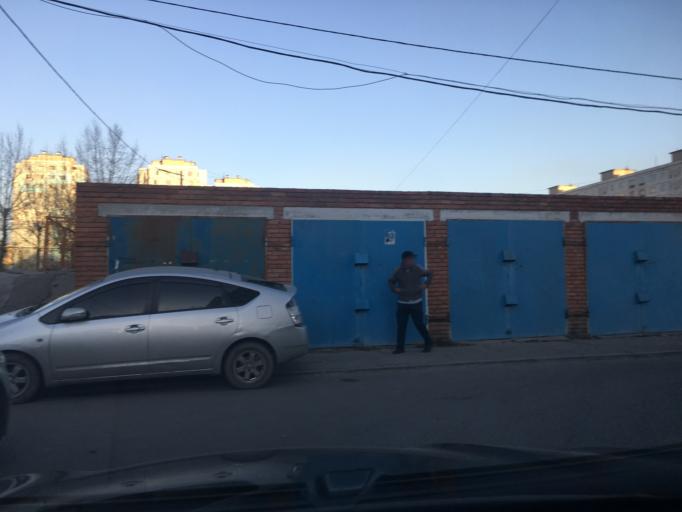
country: MN
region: Ulaanbaatar
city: Ulaanbaatar
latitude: 47.9245
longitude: 106.8853
